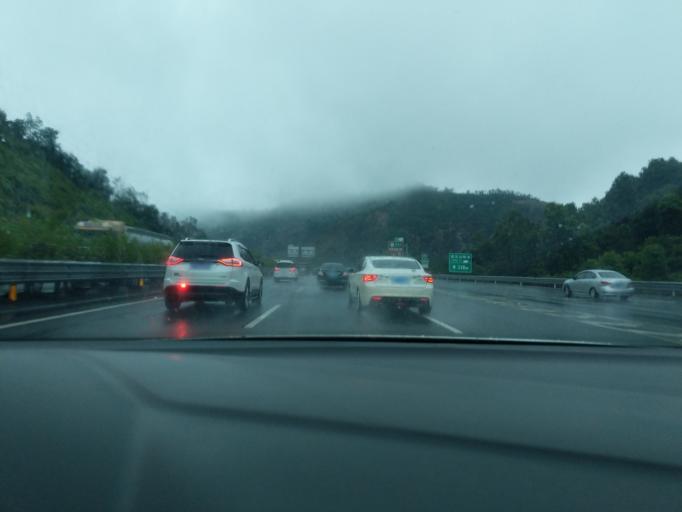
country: CN
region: Guangdong
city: Duruan
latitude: 22.5848
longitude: 113.0317
